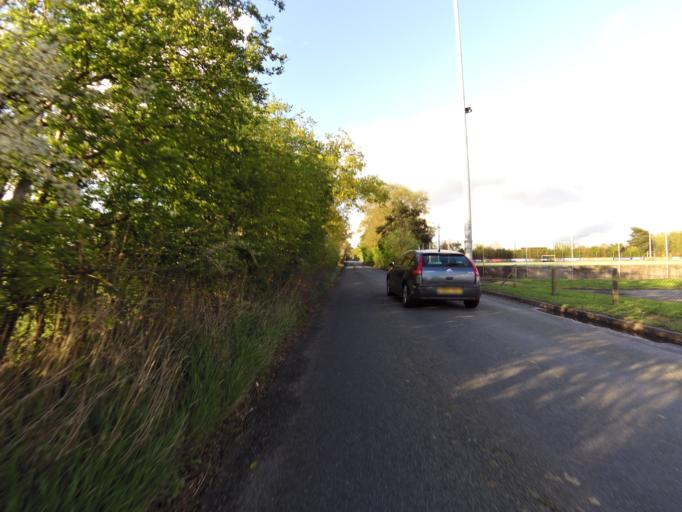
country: GB
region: England
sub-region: Suffolk
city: Ipswich
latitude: 52.0748
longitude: 1.1777
